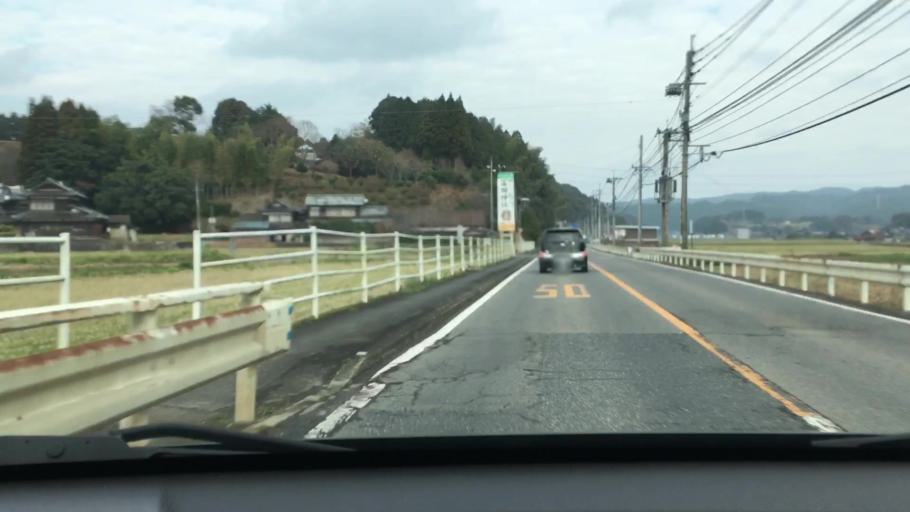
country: JP
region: Saga Prefecture
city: Imaricho-ko
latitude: 33.3009
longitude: 129.9188
